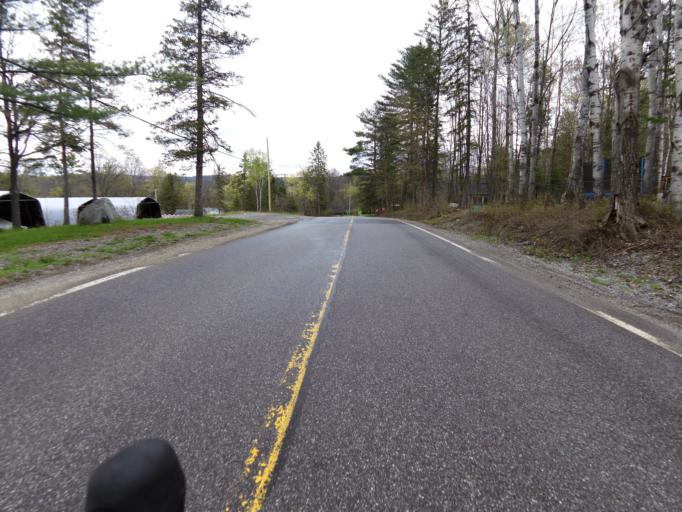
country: CA
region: Quebec
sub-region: Outaouais
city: Wakefield
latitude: 45.6014
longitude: -75.8965
